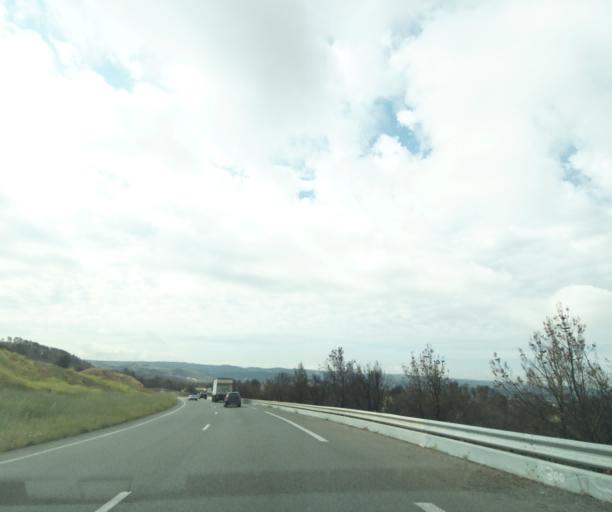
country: FR
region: Provence-Alpes-Cote d'Azur
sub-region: Departement des Bouches-du-Rhone
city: Les Pennes-Mirabeau
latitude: 43.4486
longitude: 5.2975
